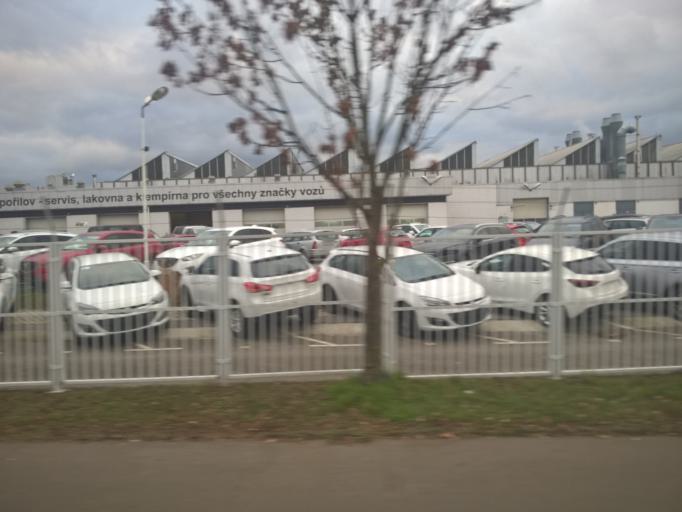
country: CZ
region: Praha
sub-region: Praha 8
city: Karlin
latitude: 50.0514
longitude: 14.4812
